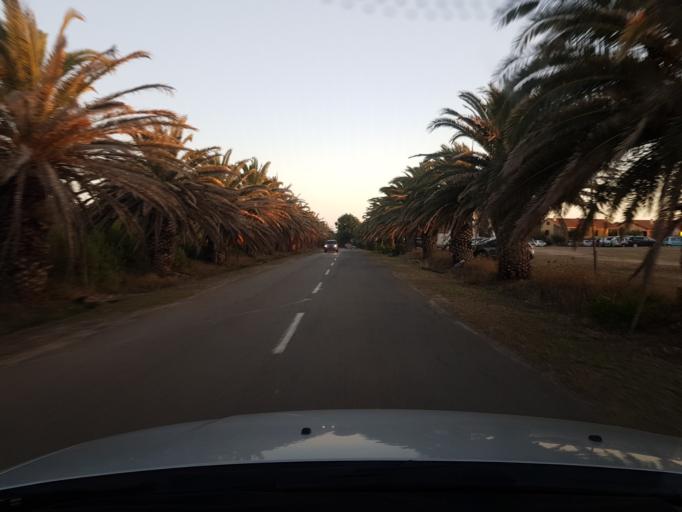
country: IT
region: Sardinia
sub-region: Provincia di Oristano
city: Riola Sardo
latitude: 40.0363
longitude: 8.3999
